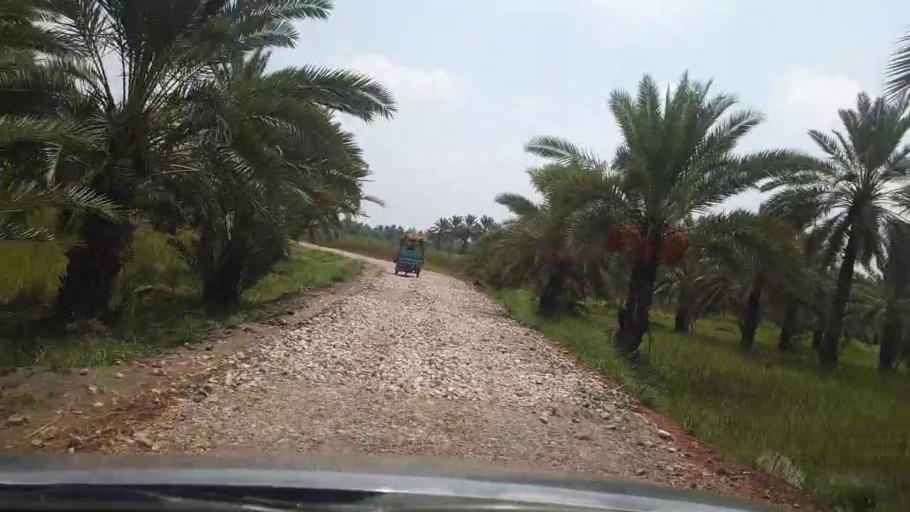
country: PK
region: Sindh
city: Pir jo Goth
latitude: 27.6188
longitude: 68.6580
